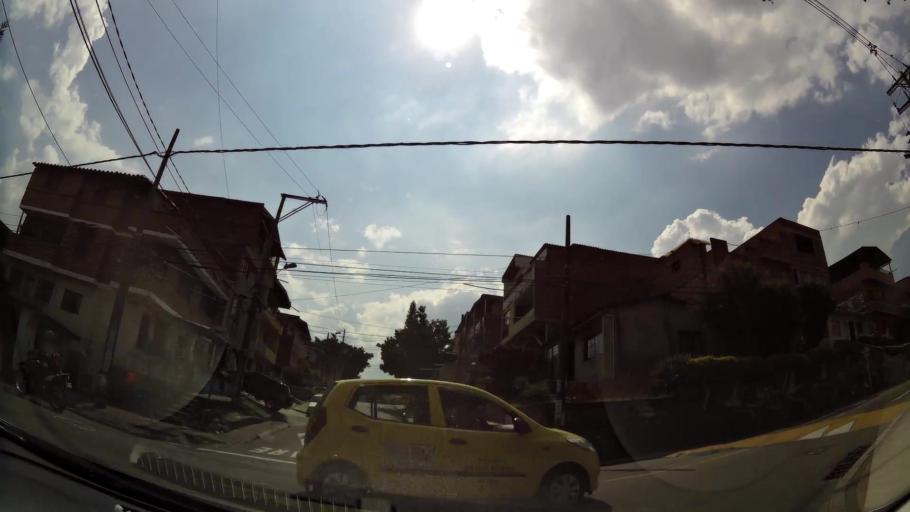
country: CO
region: Antioquia
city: Medellin
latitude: 6.2858
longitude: -75.5775
